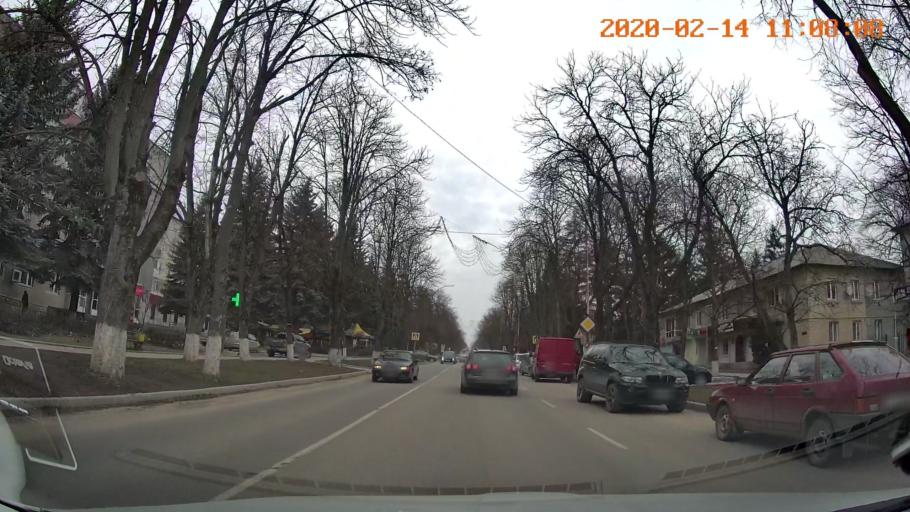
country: MD
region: Raionul Edinet
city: Edinet
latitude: 48.1708
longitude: 27.3040
